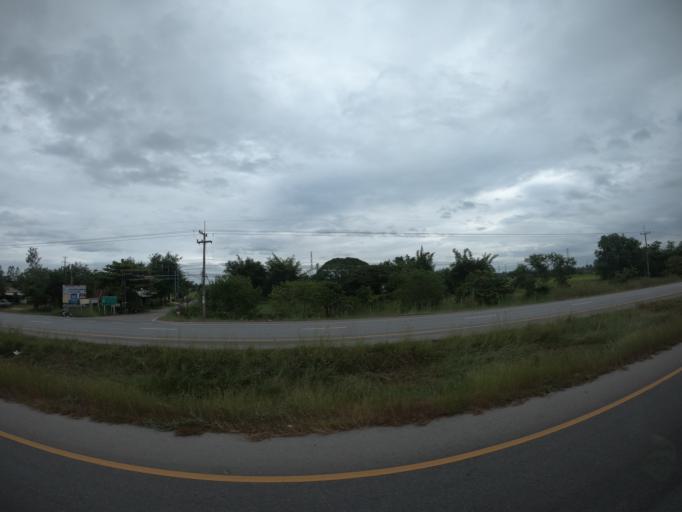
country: TH
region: Roi Et
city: Changhan
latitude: 16.1055
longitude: 103.5167
